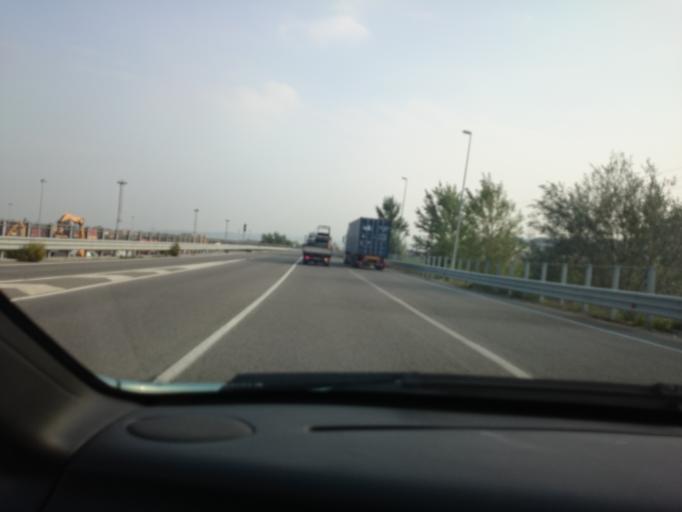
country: IT
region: Emilia-Romagna
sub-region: Provincia di Reggio Emilia
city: Veggia-Villalunga
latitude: 44.5716
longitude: 10.7504
